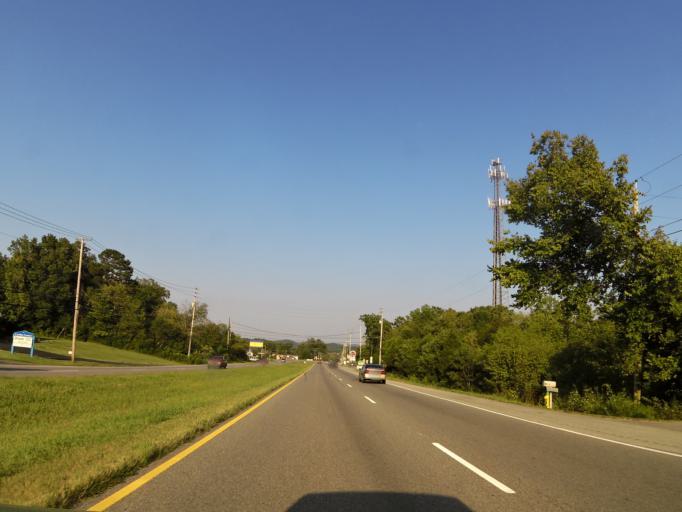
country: US
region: Tennessee
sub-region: Knox County
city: Mascot
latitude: 36.0250
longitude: -83.7400
